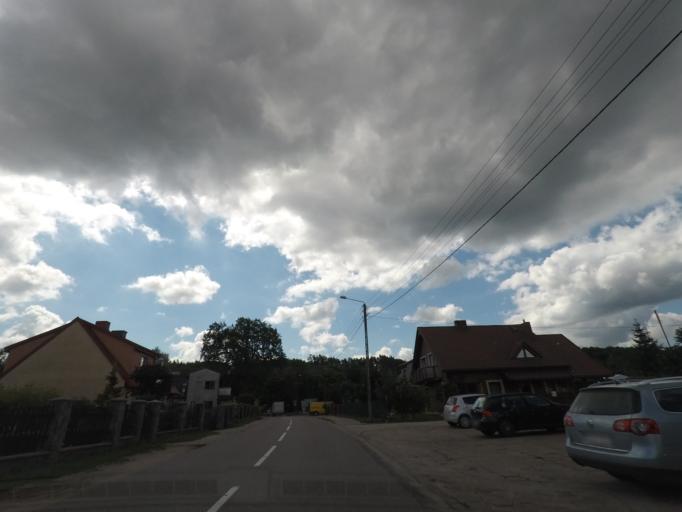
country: PL
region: Pomeranian Voivodeship
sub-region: Powiat wejherowski
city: Leczyce
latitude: 54.5744
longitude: 17.8657
